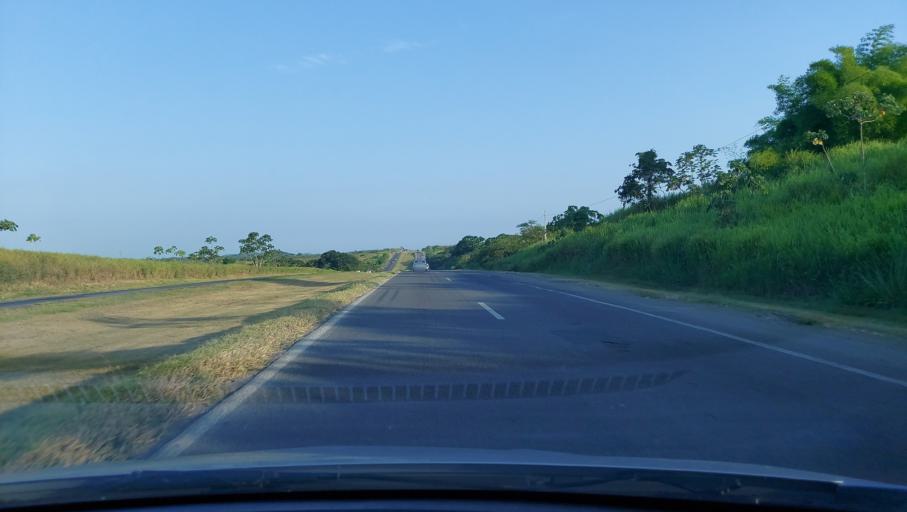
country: BR
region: Bahia
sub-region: Santo Amaro
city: Santo Amaro
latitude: -12.5159
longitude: -38.6220
